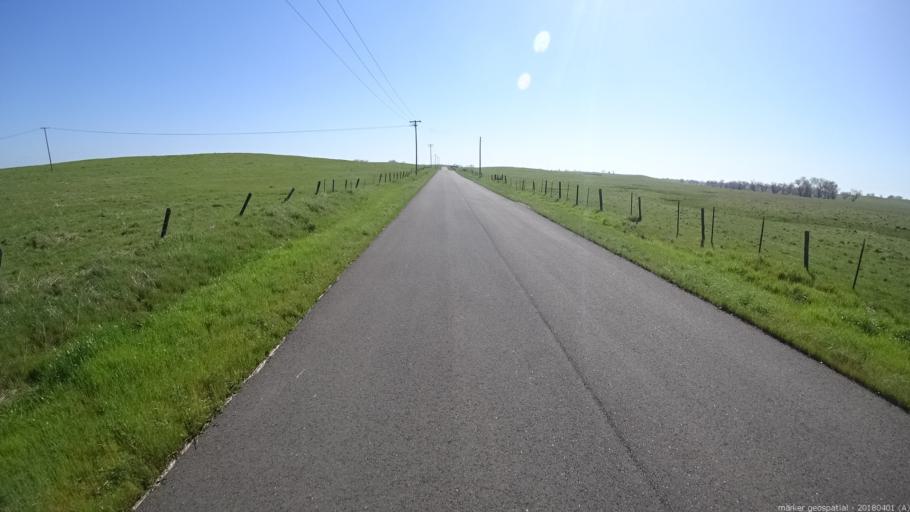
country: US
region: California
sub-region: Sacramento County
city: Rancho Murieta
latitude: 38.4652
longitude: -121.1411
